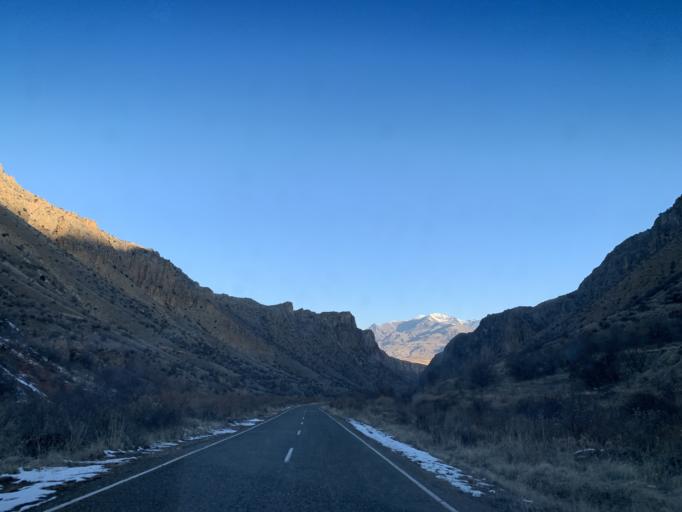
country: AM
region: Vayots' Dzori Marz
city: Areni
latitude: 39.7014
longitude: 45.2094
